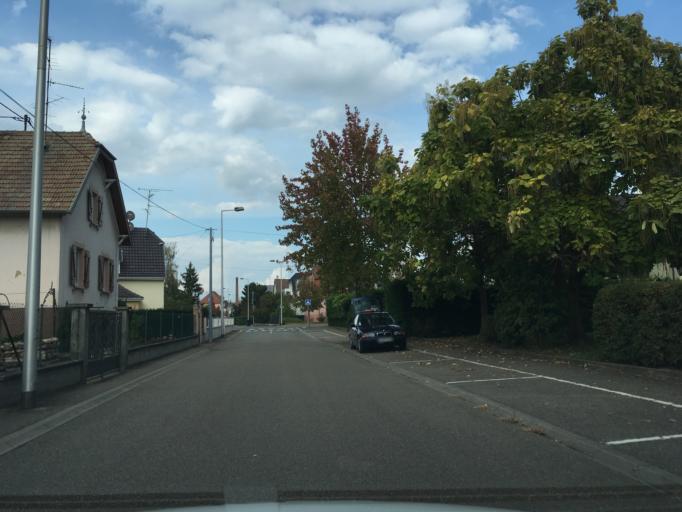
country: FR
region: Alsace
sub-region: Departement du Haut-Rhin
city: Colmar
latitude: 48.0714
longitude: 7.3680
